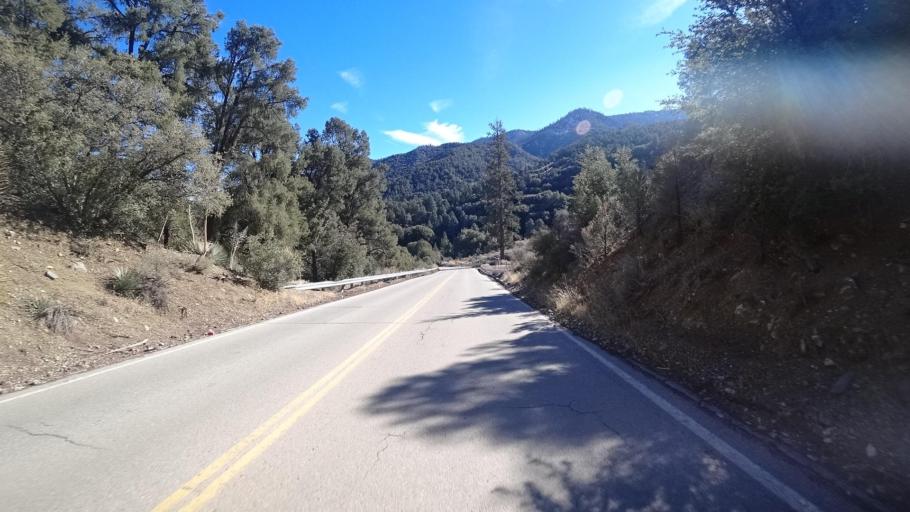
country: US
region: California
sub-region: Kern County
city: Pine Mountain Club
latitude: 34.8530
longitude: -119.1330
